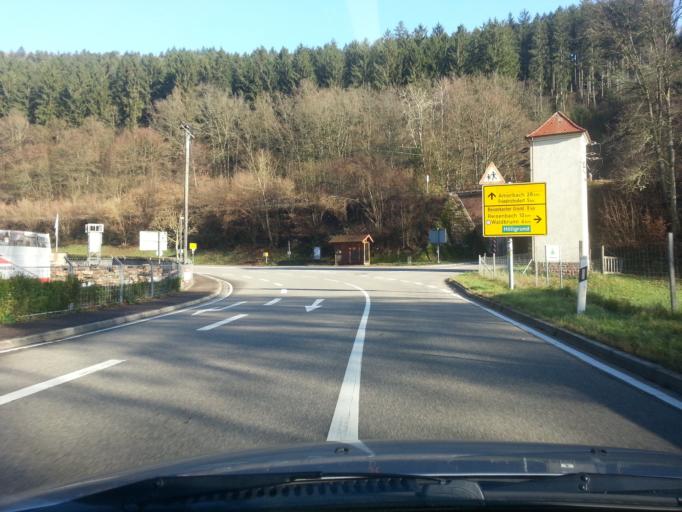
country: DE
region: Baden-Wuerttemberg
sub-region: Karlsruhe Region
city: Eberbach
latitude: 49.4945
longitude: 9.0454
